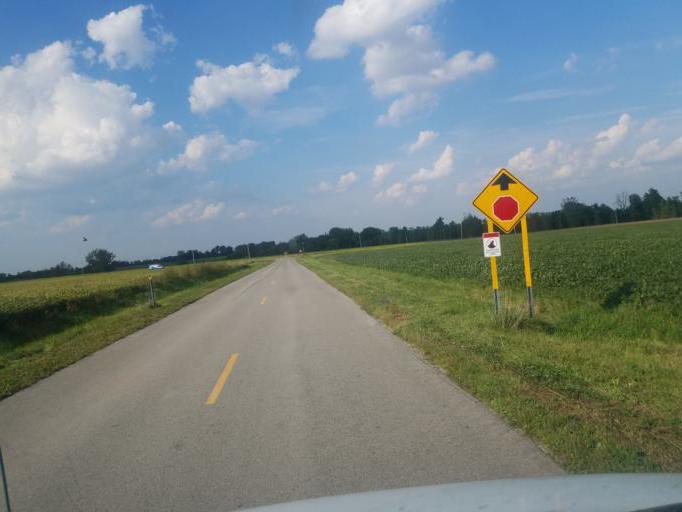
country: US
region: Ohio
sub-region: Hancock County
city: Arlington
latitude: 40.8892
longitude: -83.5684
